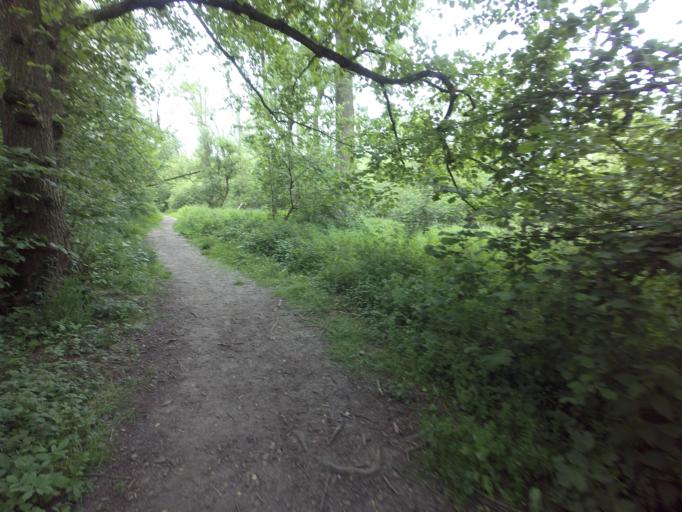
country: NL
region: Limburg
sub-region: Gemeente Voerendaal
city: Ubachsberg
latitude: 50.8240
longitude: 5.9097
